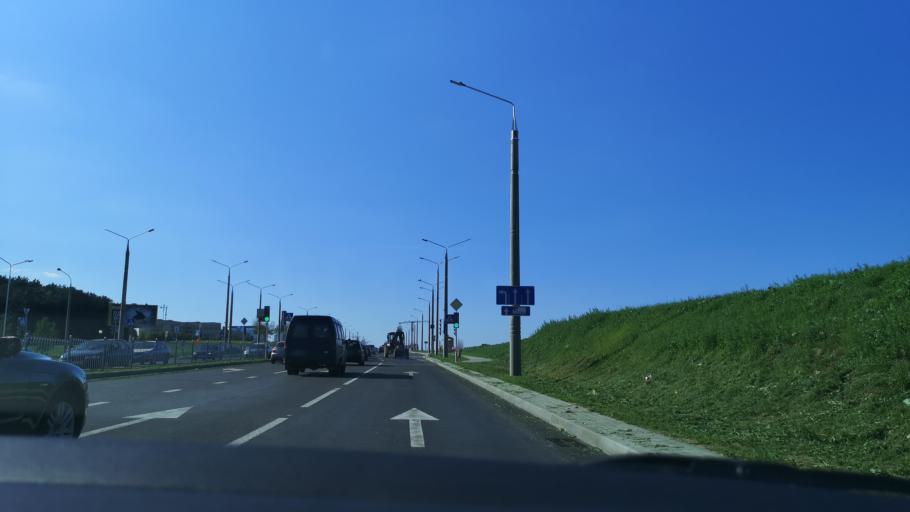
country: BY
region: Grodnenskaya
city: Hrodna
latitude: 53.6470
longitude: 23.8676
